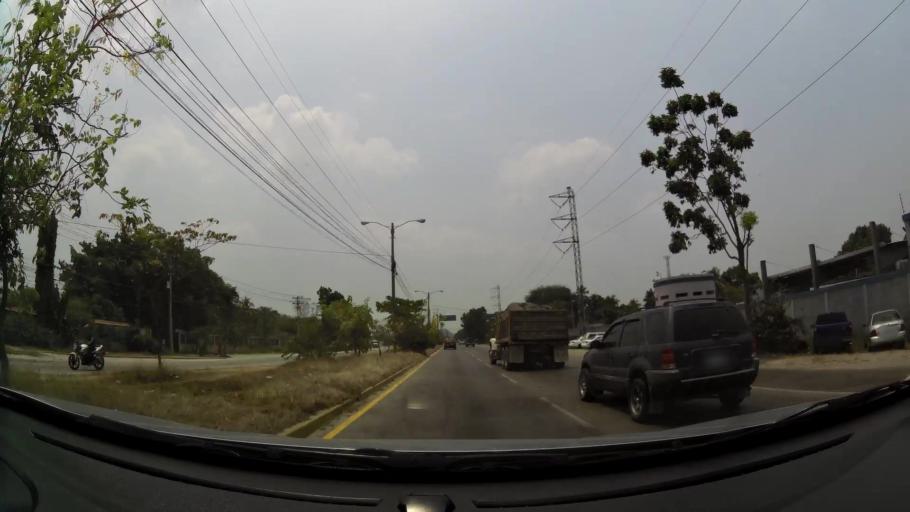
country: HN
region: Cortes
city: San Pedro Sula
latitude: 15.4763
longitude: -87.9728
